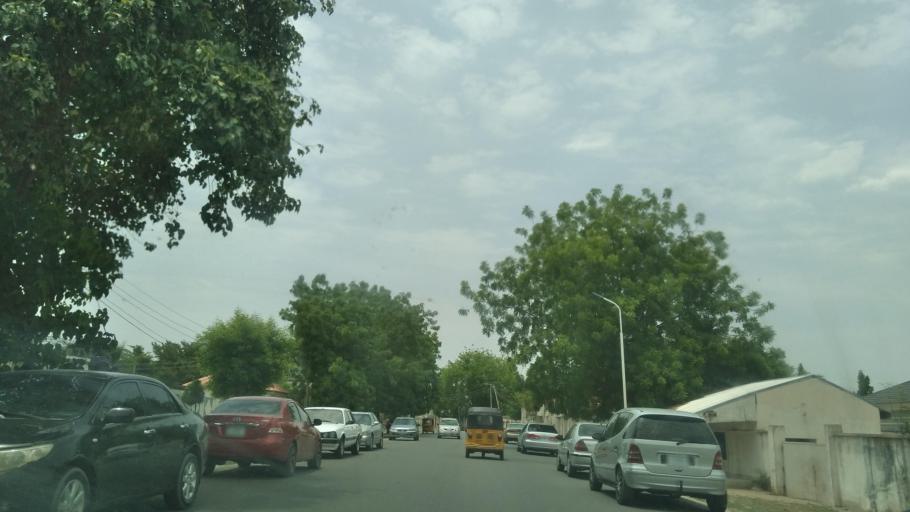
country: NG
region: Borno
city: Maiduguri
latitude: 11.8072
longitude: 13.1596
